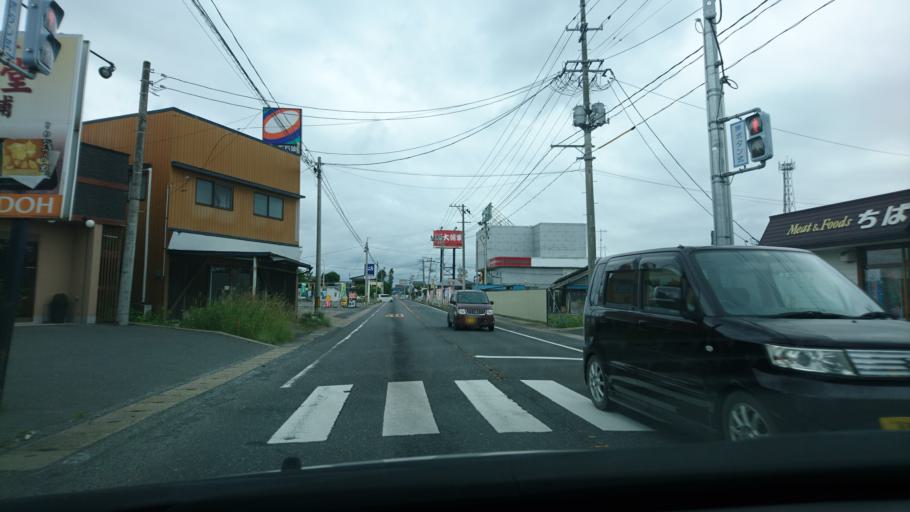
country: JP
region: Miyagi
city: Wakuya
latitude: 38.7228
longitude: 141.2610
